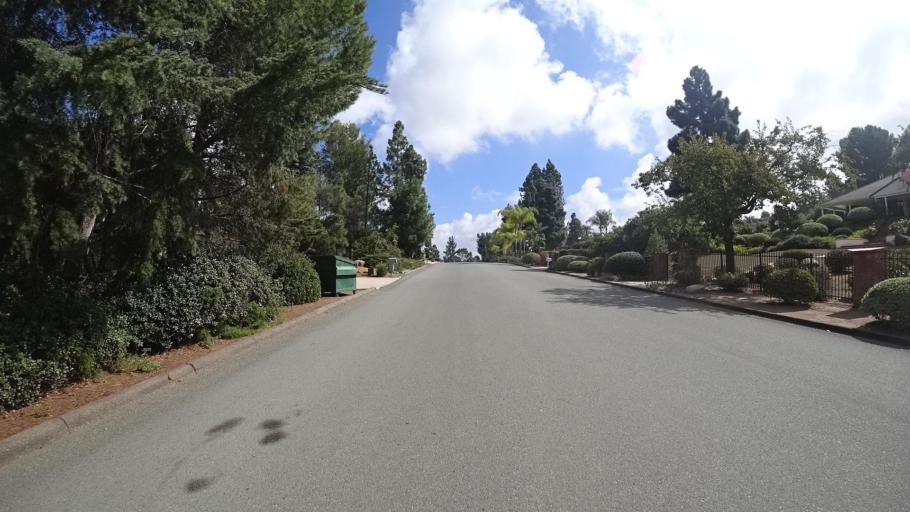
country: US
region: California
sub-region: San Diego County
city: Granite Hills
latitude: 32.7797
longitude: -116.9013
